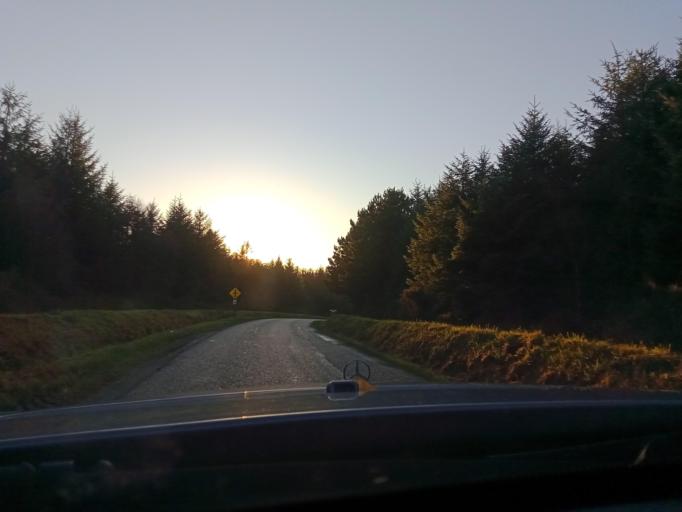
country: IE
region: Munster
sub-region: Waterford
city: Waterford
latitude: 52.3702
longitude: -7.1064
